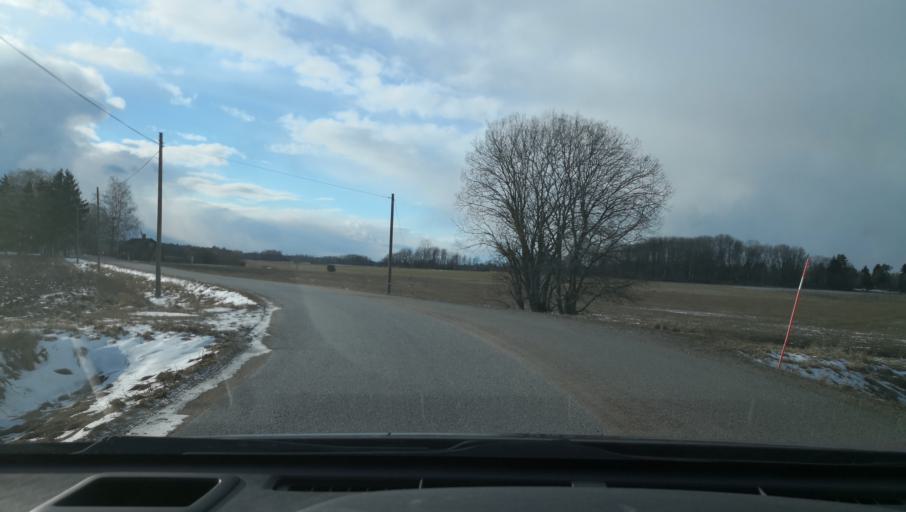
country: SE
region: Uppsala
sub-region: Enkopings Kommun
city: Irsta
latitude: 59.6978
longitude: 16.9508
